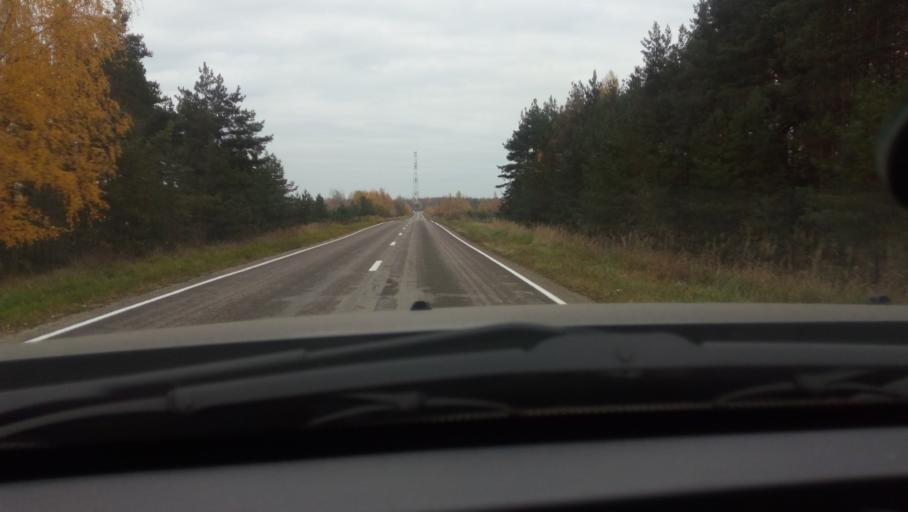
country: RU
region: Moskovskaya
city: Avsyunino
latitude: 55.5976
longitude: 39.2351
